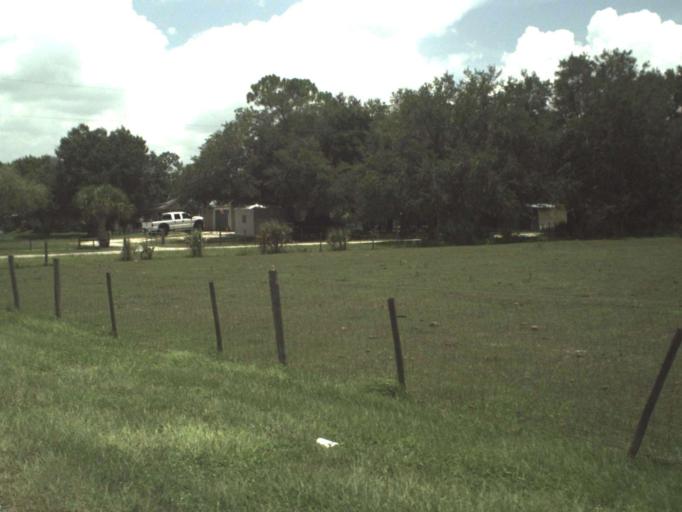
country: US
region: Florida
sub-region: Saint Lucie County
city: Fort Pierce South
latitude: 27.3744
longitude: -80.4366
